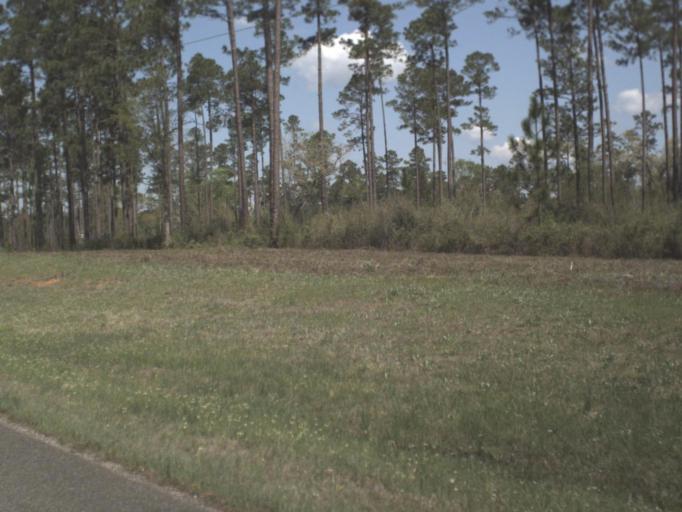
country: US
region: Florida
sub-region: Santa Rosa County
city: Point Baker
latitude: 30.8771
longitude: -86.9465
